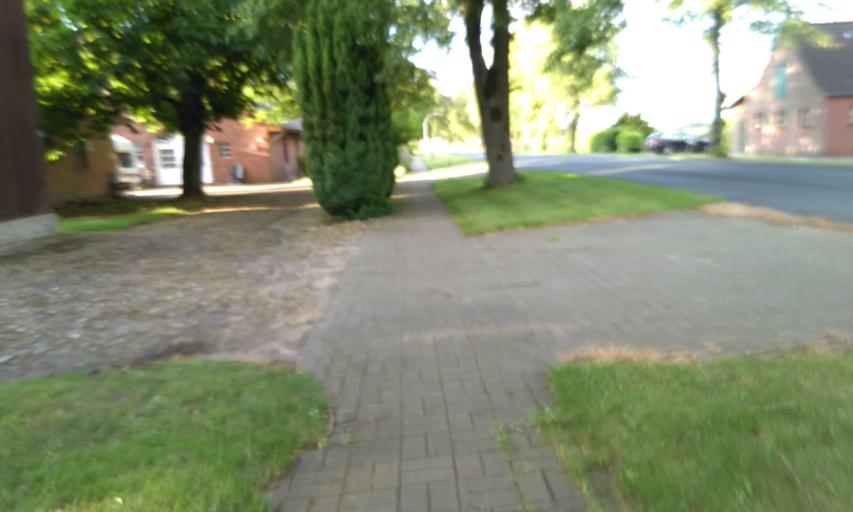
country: DE
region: Lower Saxony
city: Anderlingen
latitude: 53.3795
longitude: 9.3076
